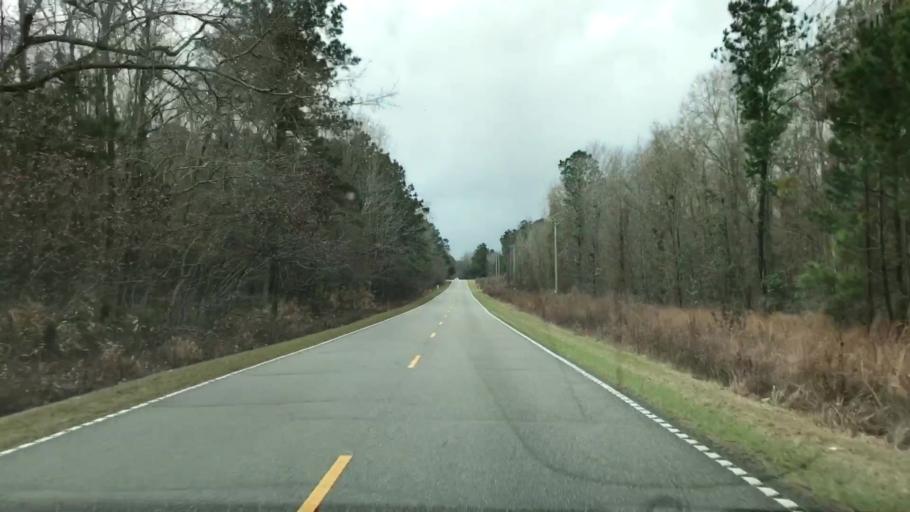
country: US
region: South Carolina
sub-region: Florence County
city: Johnsonville
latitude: 33.6643
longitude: -79.4082
